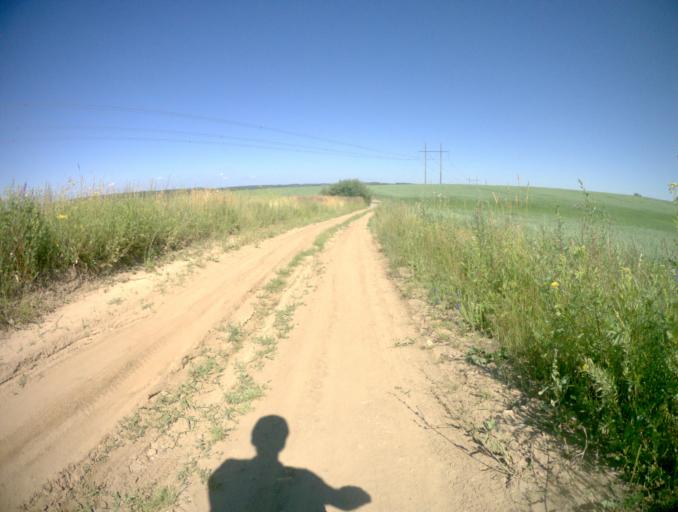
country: RU
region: Nizjnij Novgorod
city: Gorbatov
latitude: 56.0807
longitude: 43.1371
